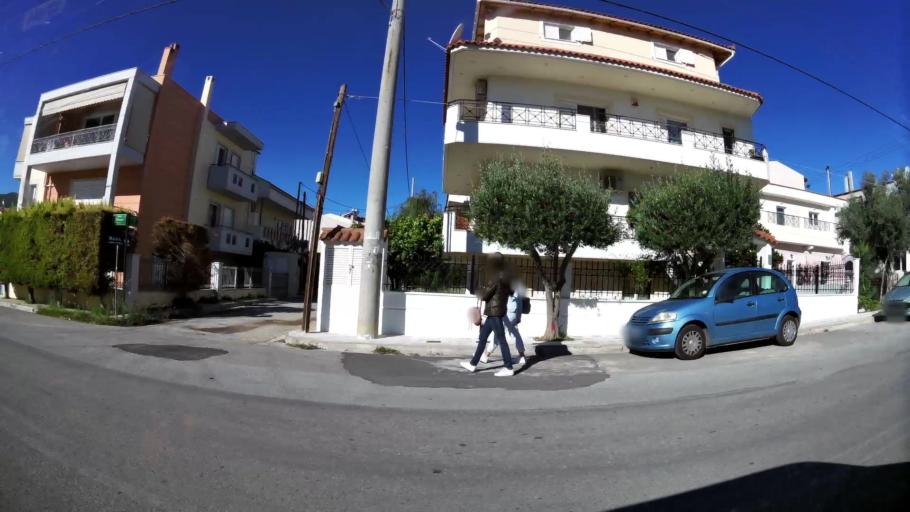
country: GR
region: Attica
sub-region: Nomarchia Anatolikis Attikis
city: Gerakas
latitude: 38.0135
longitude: 23.8578
